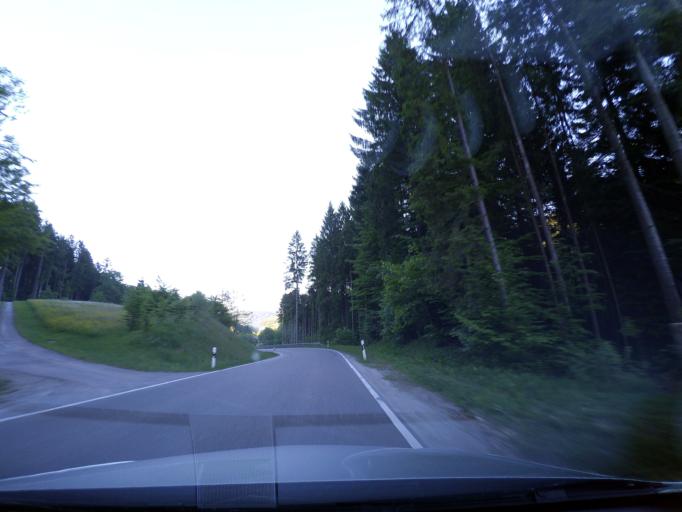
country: DE
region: Baden-Wuerttemberg
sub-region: Regierungsbezirk Stuttgart
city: Kaisersbach
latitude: 48.9570
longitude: 9.6072
